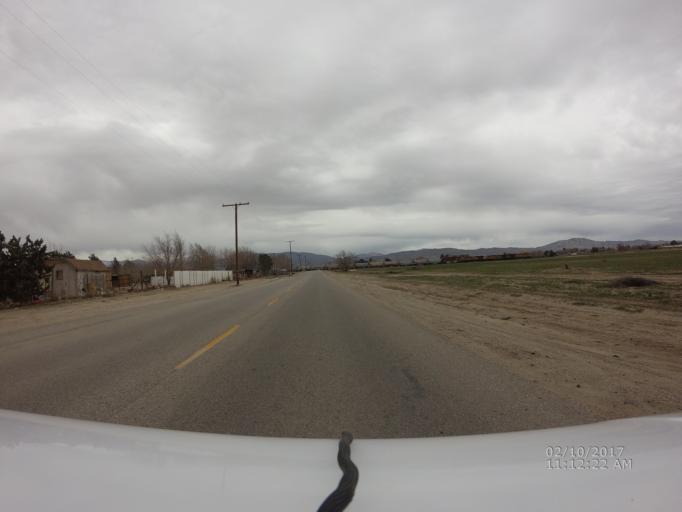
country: US
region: California
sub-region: Los Angeles County
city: Littlerock
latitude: 34.5462
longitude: -117.9582
